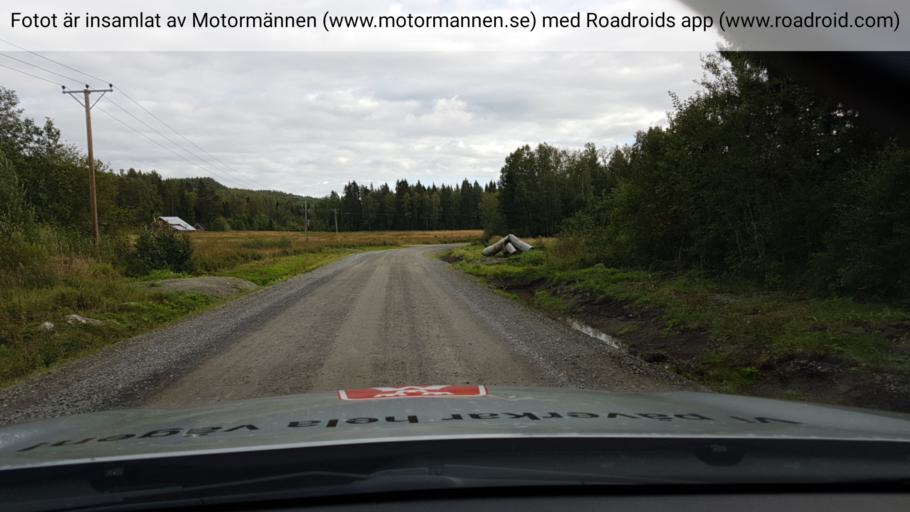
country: SE
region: Jaemtland
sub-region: Ragunda Kommun
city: Hammarstrand
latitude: 62.9368
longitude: 16.1286
